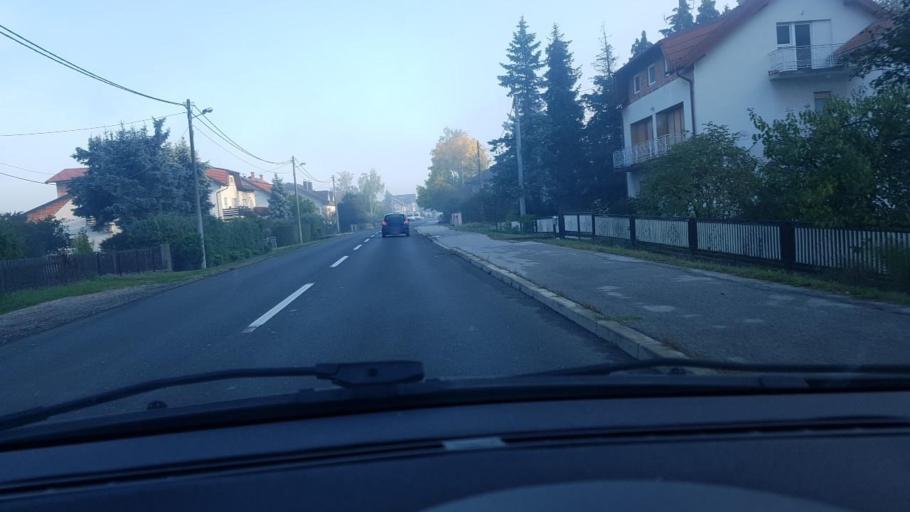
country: HR
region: Grad Zagreb
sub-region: Sesvete
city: Sesvete
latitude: 45.8468
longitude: 16.1102
